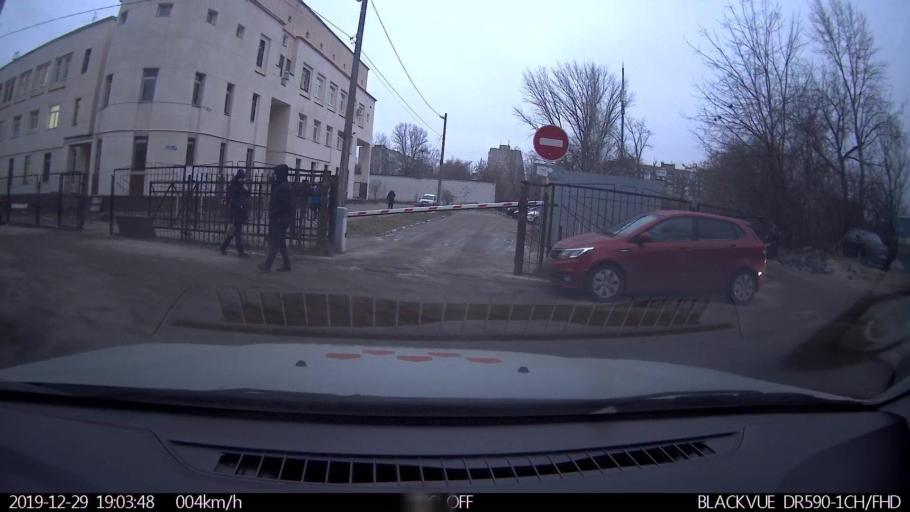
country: RU
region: Nizjnij Novgorod
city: Neklyudovo
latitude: 56.3576
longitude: 43.8569
